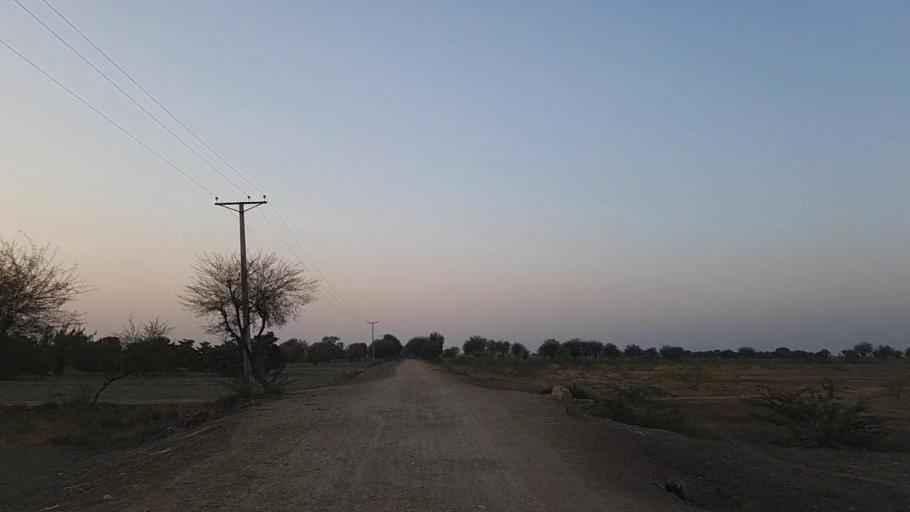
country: PK
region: Sindh
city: Naukot
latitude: 24.8887
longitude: 69.3646
